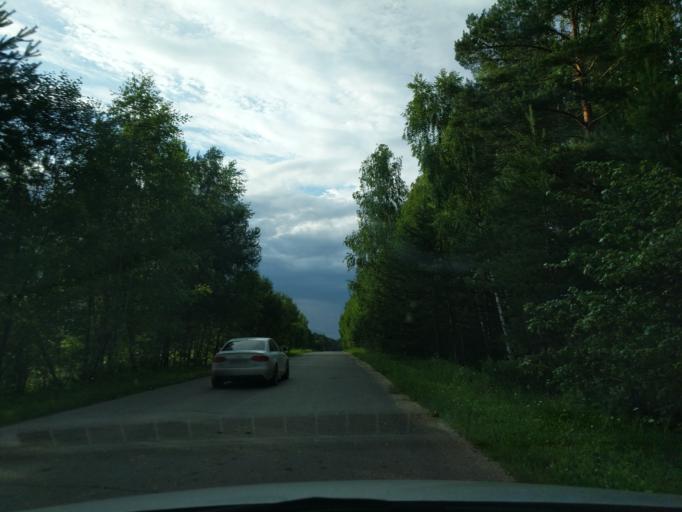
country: RU
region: Kaluga
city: Myatlevo
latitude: 54.8183
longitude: 35.6749
